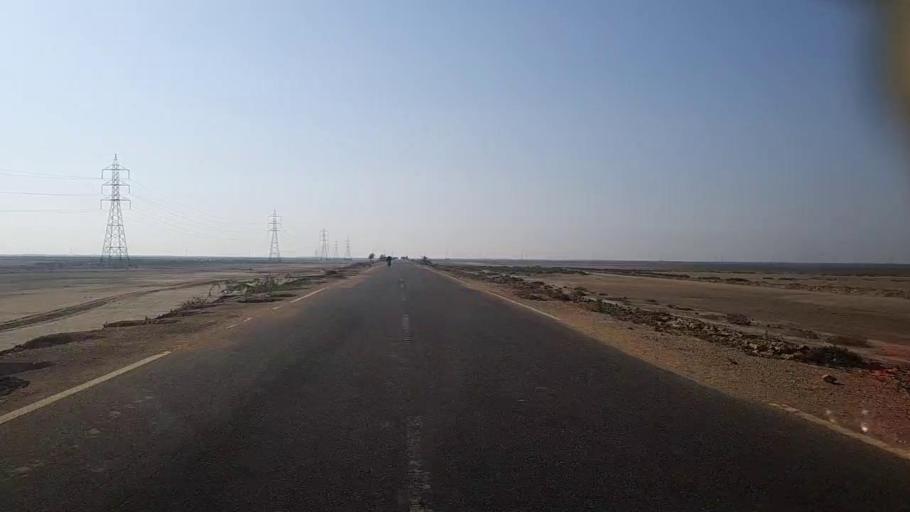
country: PK
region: Sindh
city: Mirpur Sakro
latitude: 24.6080
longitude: 67.4972
